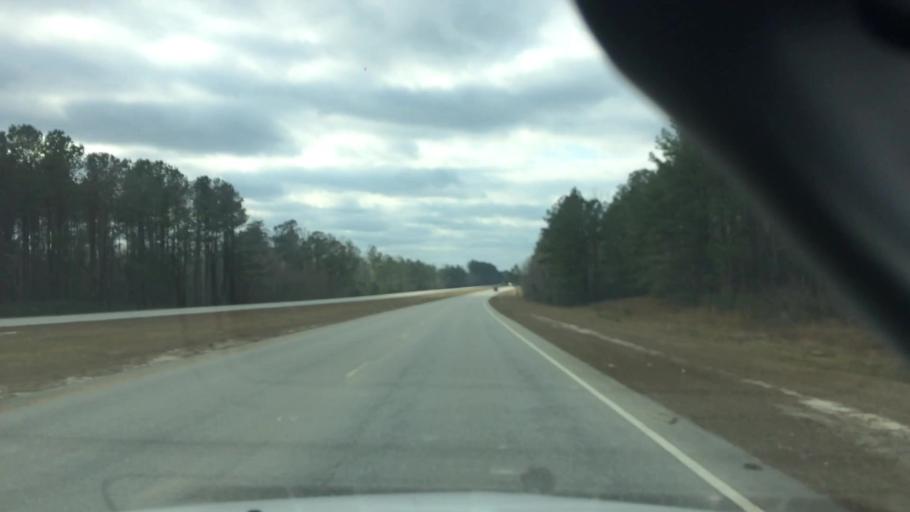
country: US
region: North Carolina
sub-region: Brunswick County
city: Bolivia
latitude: 34.0681
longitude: -78.1790
